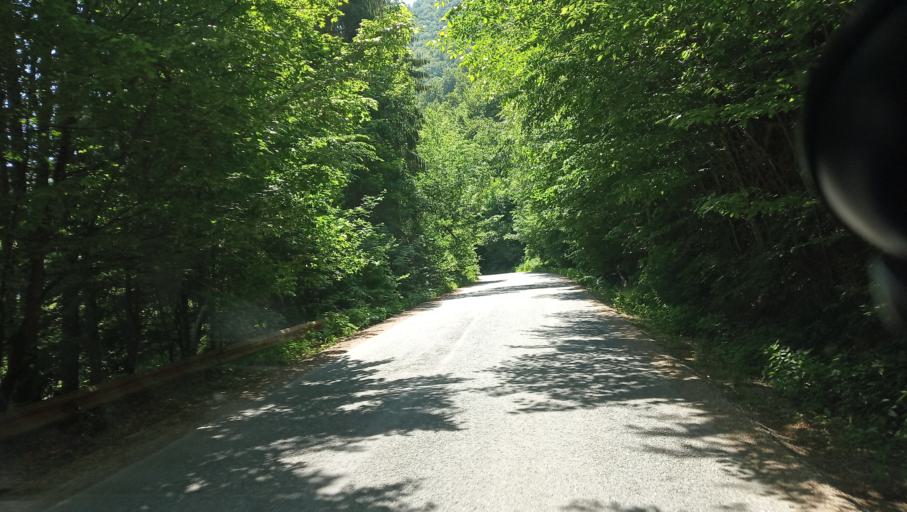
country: RO
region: Cluj
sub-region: Comuna Capusu Mare
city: Capusu Mare
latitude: 46.7144
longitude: 23.2680
